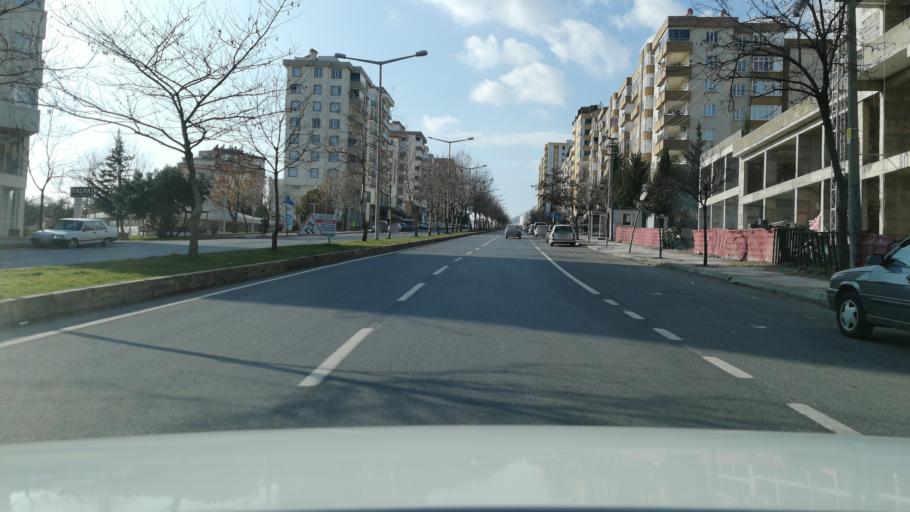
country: TR
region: Kahramanmaras
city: Kahramanmaras
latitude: 37.5930
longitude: 36.8979
